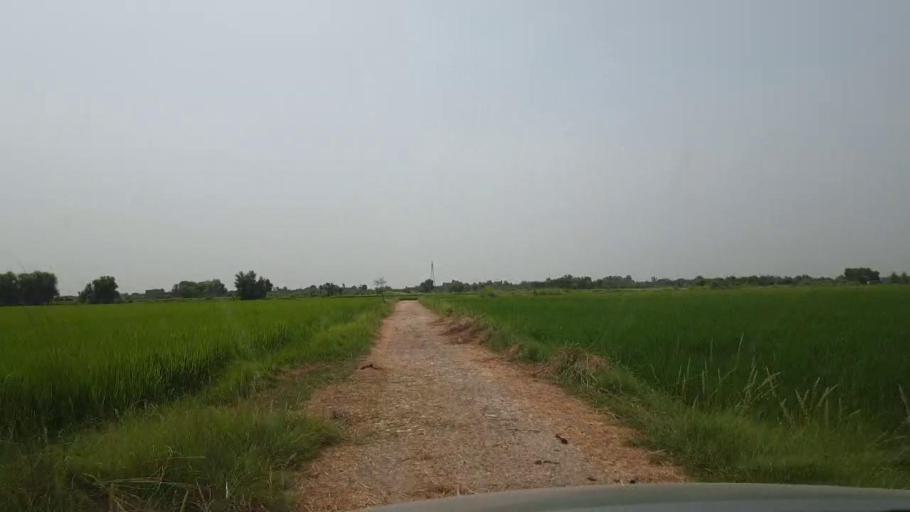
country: PK
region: Sindh
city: Madeji
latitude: 27.7912
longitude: 68.5381
